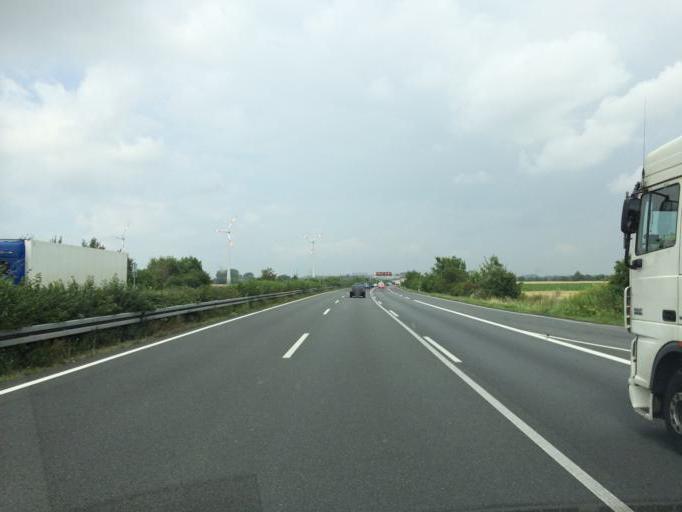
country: DE
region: Lower Saxony
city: Haste
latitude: 52.3476
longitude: 9.4225
